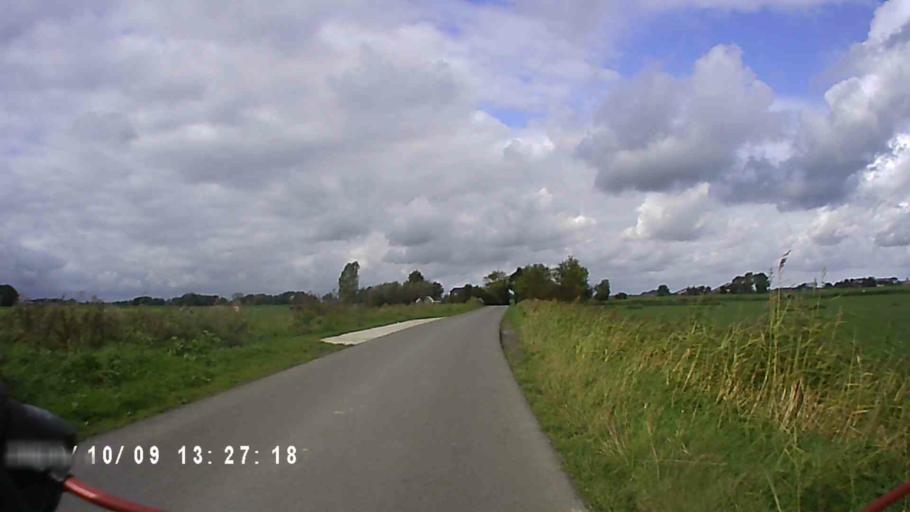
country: NL
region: Groningen
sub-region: Gemeente Zuidhorn
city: Aduard
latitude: 53.2671
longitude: 6.4607
